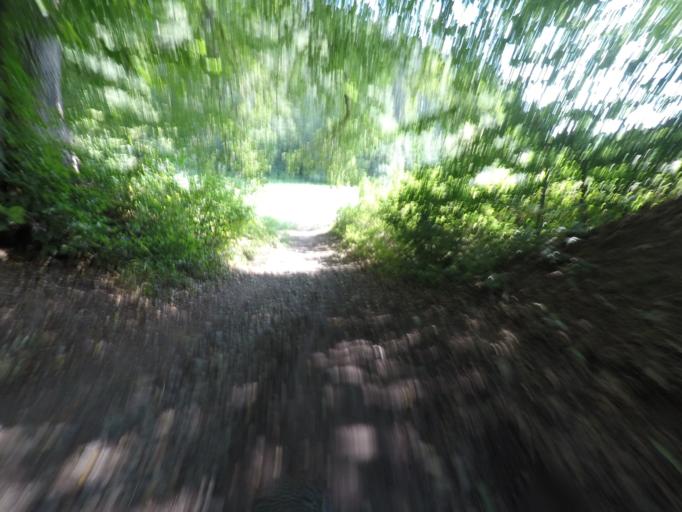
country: DE
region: Baden-Wuerttemberg
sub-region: Regierungsbezirk Stuttgart
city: Steinenbronn
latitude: 48.6972
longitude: 9.1072
